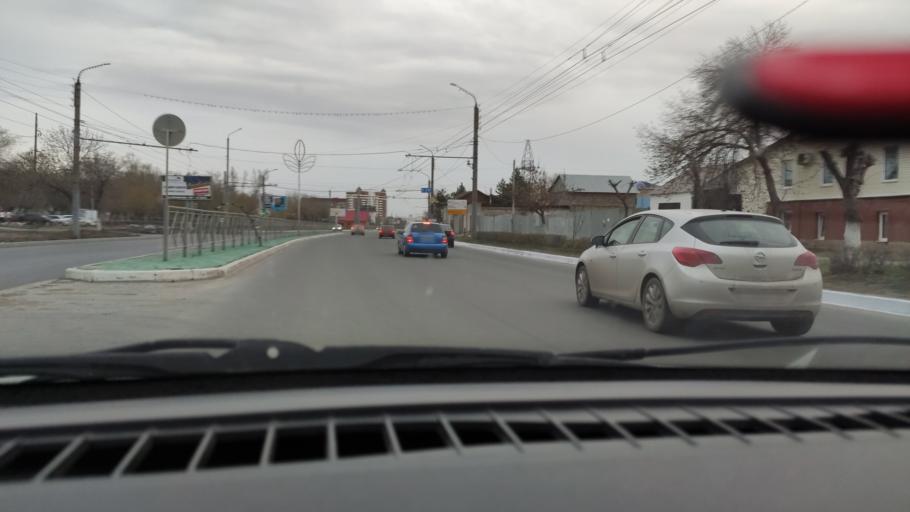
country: RU
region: Orenburg
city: Orenburg
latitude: 51.7867
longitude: 55.1064
